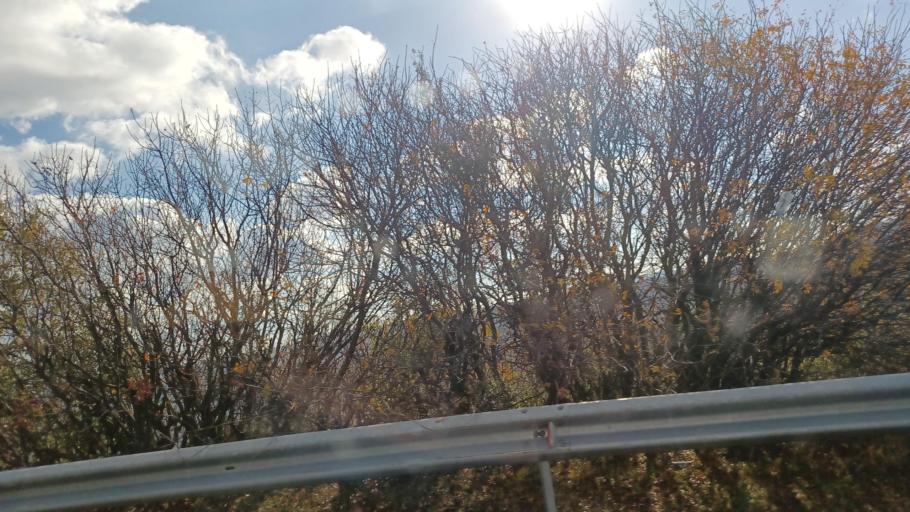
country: CY
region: Limassol
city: Pachna
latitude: 34.8432
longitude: 32.6936
